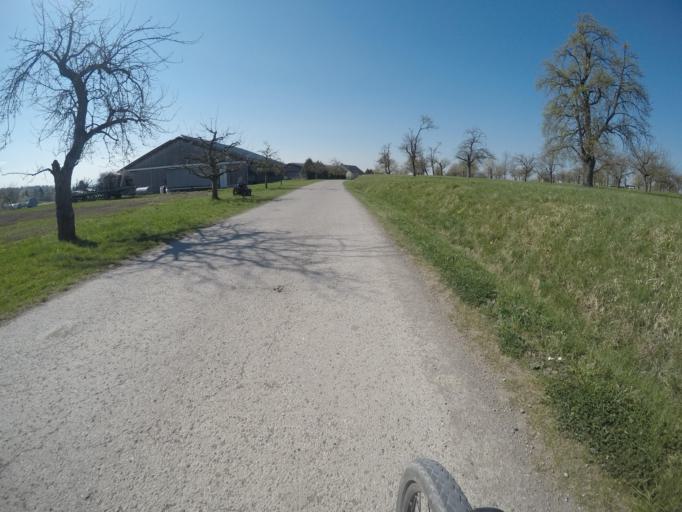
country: DE
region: Baden-Wuerttemberg
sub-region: Regierungsbezirk Stuttgart
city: Herrenberg
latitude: 48.5665
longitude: 8.9231
